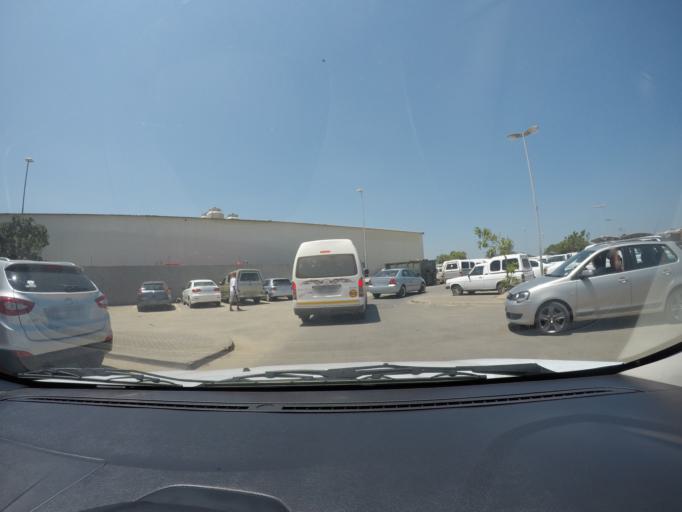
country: ZA
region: KwaZulu-Natal
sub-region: uThungulu District Municipality
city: eSikhawini
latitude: -28.8729
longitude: 31.9002
